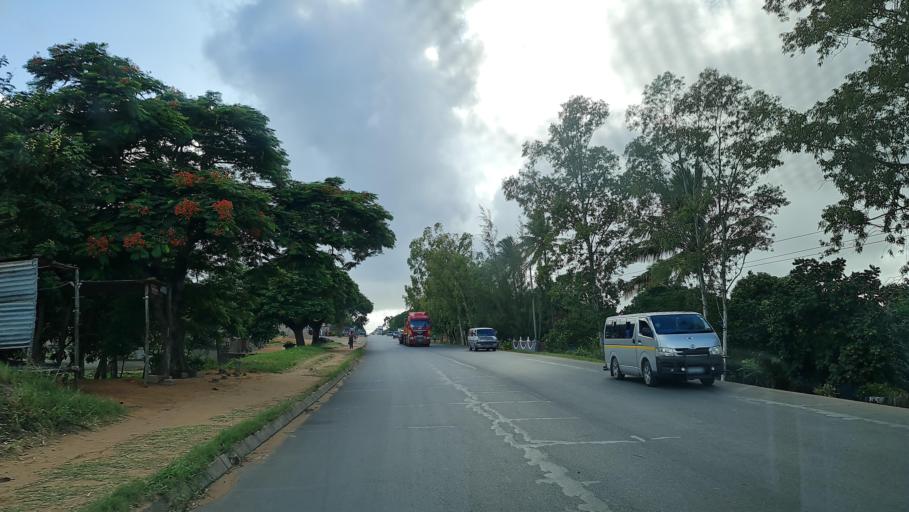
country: MZ
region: Gaza
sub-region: Xai-Xai District
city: Xai-Xai
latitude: -25.0573
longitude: 33.6792
